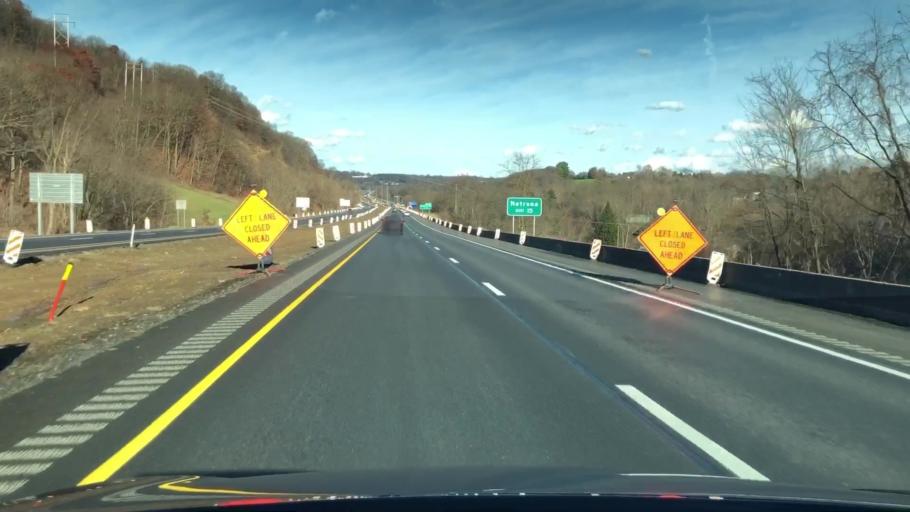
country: US
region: Pennsylvania
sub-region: Allegheny County
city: Brackenridge
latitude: 40.6222
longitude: -79.7445
